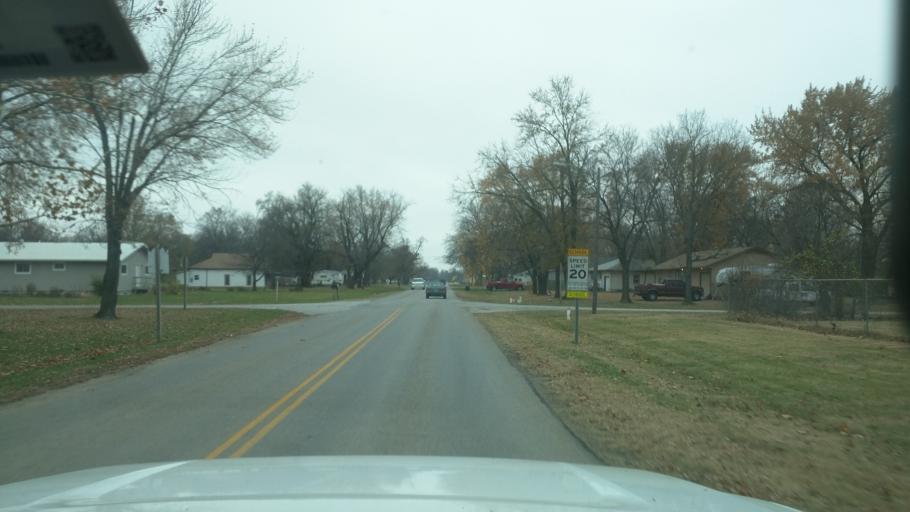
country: US
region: Kansas
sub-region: Lyon County
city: Emporia
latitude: 38.5106
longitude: -96.2620
